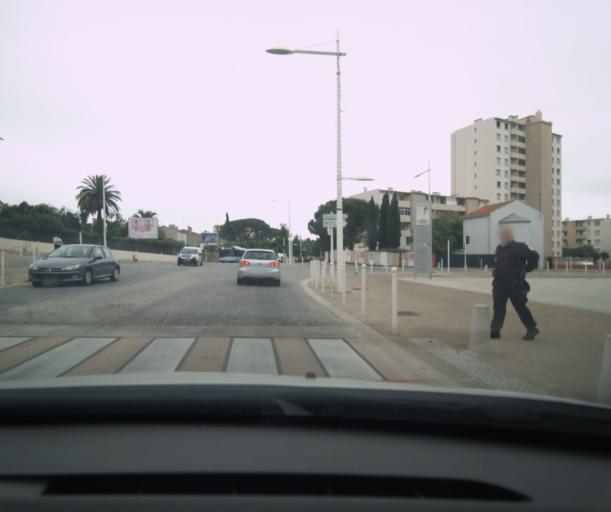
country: FR
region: Provence-Alpes-Cote d'Azur
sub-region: Departement du Var
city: La Valette-du-Var
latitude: 43.1226
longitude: 5.9816
